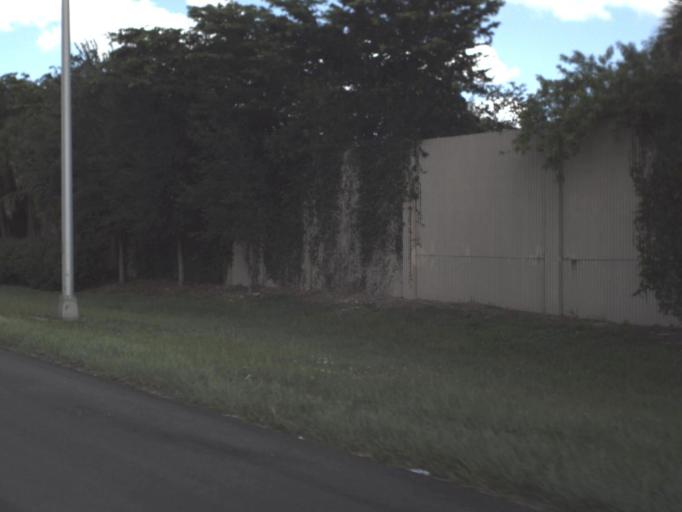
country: US
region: Florida
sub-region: Broward County
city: Tamarac
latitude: 26.2081
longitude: -80.2963
